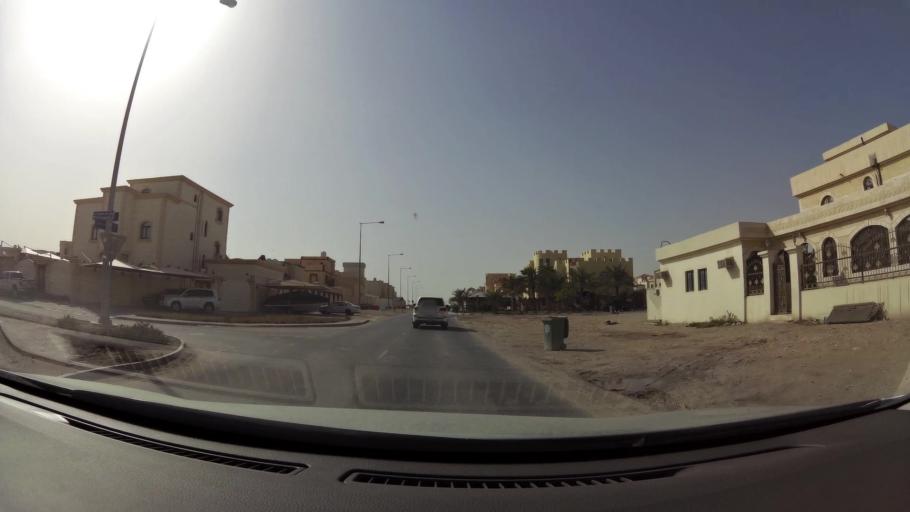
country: QA
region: Baladiyat ar Rayyan
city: Ar Rayyan
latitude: 25.3411
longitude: 51.4222
